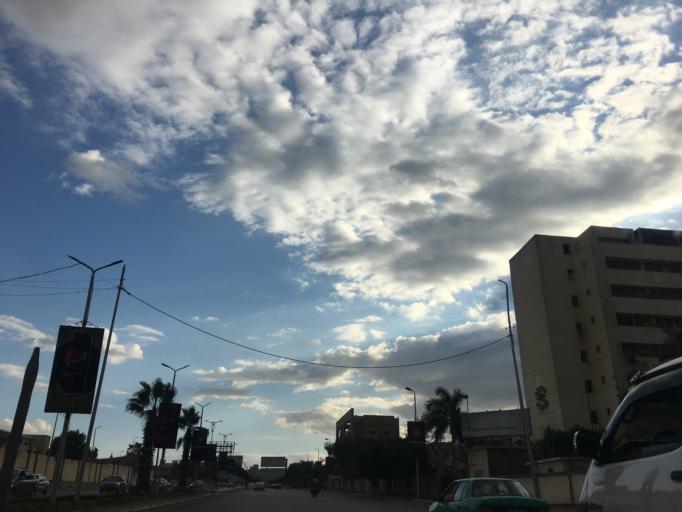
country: EG
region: Muhafazat al Qahirah
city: Cairo
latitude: 30.0529
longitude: 31.3073
